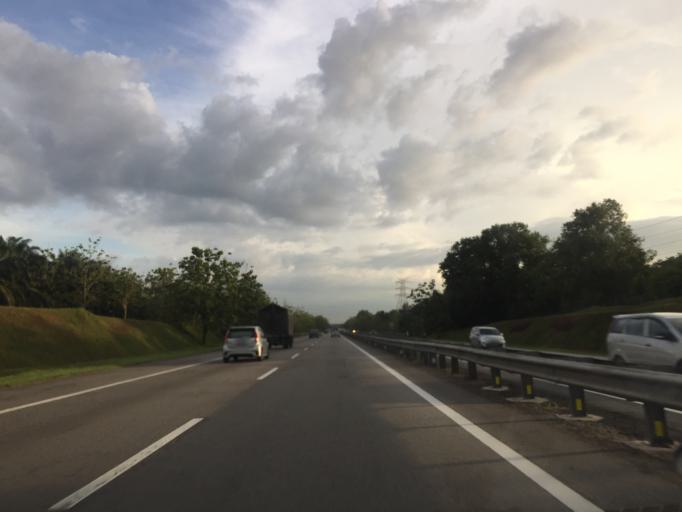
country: MY
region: Kedah
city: Gurun
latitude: 5.7822
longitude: 100.5025
